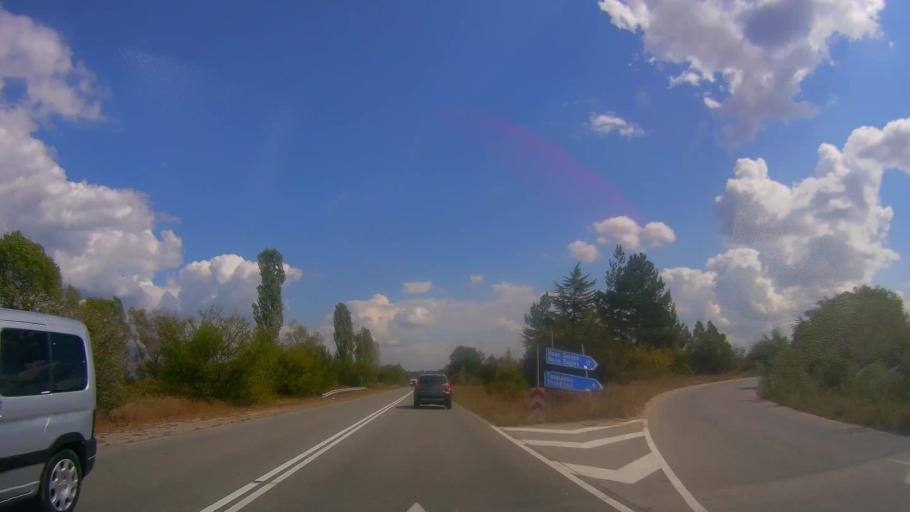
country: BG
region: Sliven
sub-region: Obshtina Tvurditsa
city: Tvurditsa
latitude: 42.6516
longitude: 25.9749
